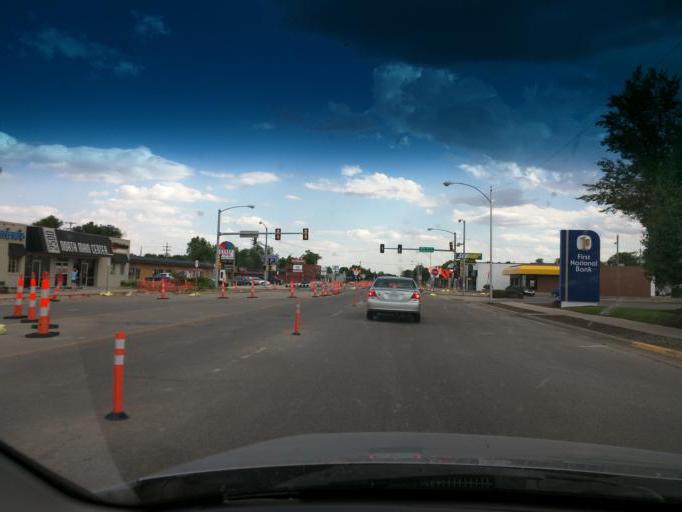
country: US
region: Kansas
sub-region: Reno County
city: Hutchinson
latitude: 38.0816
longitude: -97.9320
